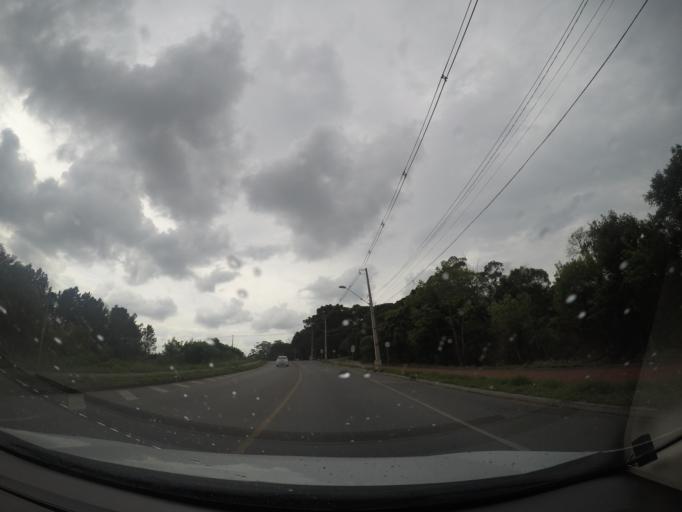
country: BR
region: Parana
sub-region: Sao Jose Dos Pinhais
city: Sao Jose dos Pinhais
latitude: -25.5457
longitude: -49.2420
